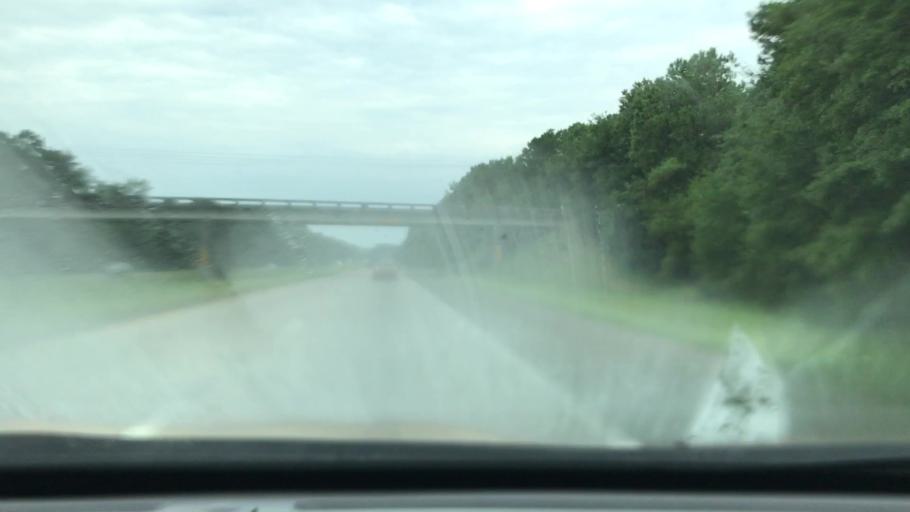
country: US
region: South Carolina
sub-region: Colleton County
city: Walterboro
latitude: 32.8401
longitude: -80.7404
